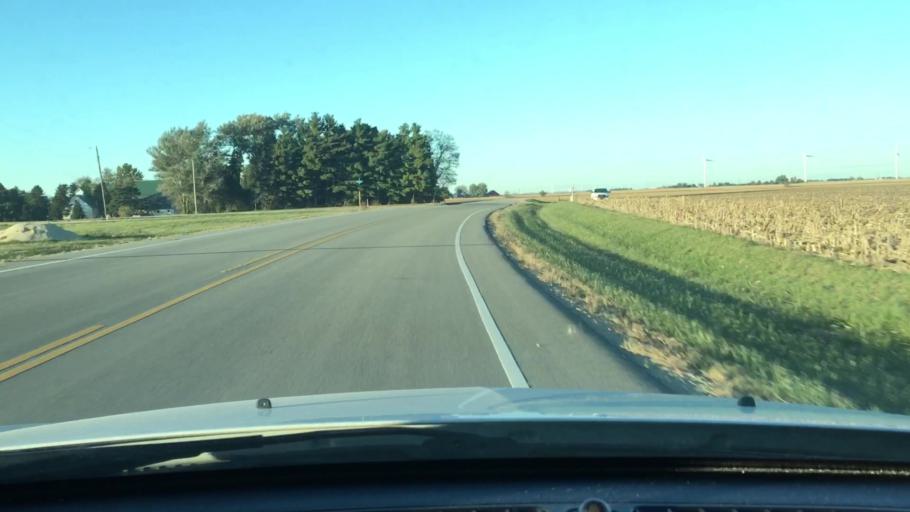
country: US
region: Illinois
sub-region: DeKalb County
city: Waterman
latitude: 41.8040
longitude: -88.8870
